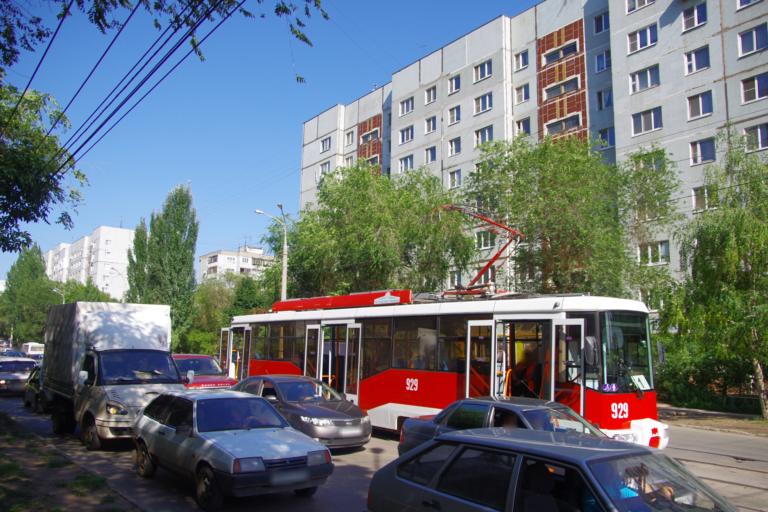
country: RU
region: Samara
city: Samara
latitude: 53.1921
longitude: 50.1427
